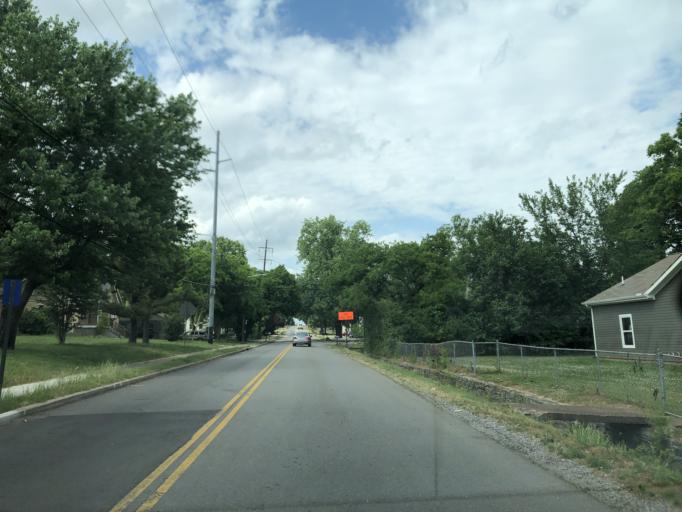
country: US
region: Tennessee
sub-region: Davidson County
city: Goodlettsville
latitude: 36.2672
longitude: -86.7035
